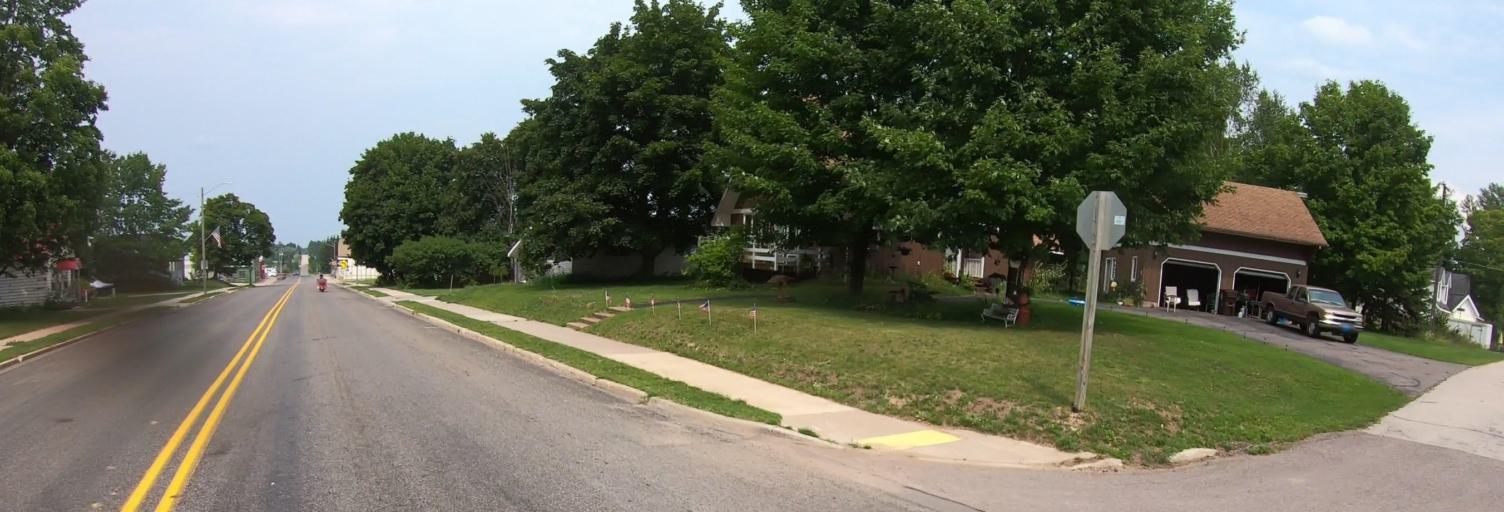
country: US
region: Michigan
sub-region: Alger County
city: Munising
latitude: 46.3449
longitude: -86.9287
